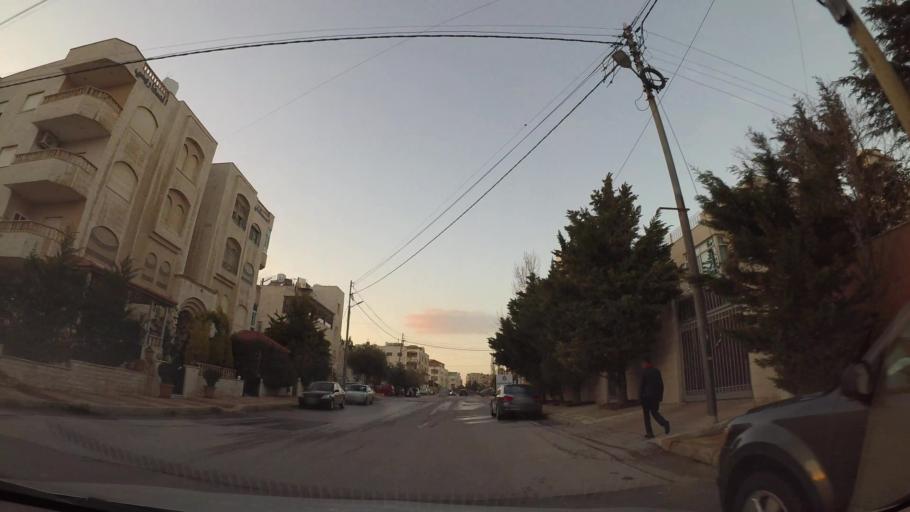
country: JO
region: Amman
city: Al Jubayhah
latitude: 32.0013
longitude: 35.8522
